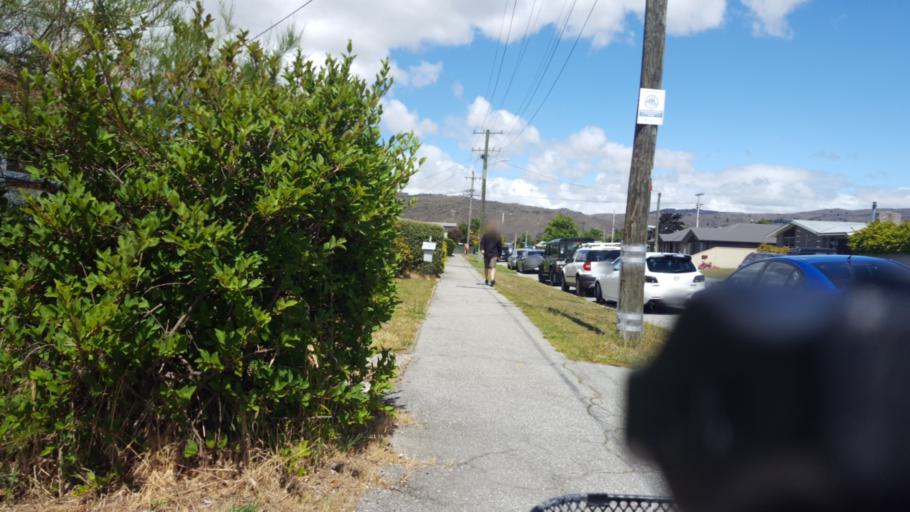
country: NZ
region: Otago
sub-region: Queenstown-Lakes District
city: Wanaka
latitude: -45.2438
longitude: 169.3897
